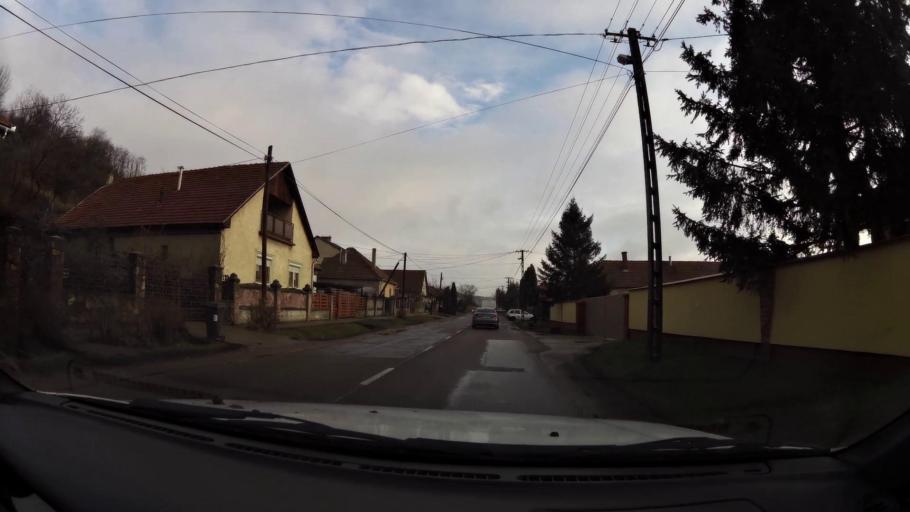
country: HU
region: Borsod-Abauj-Zemplen
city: Mucsony
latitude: 48.2674
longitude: 20.6884
